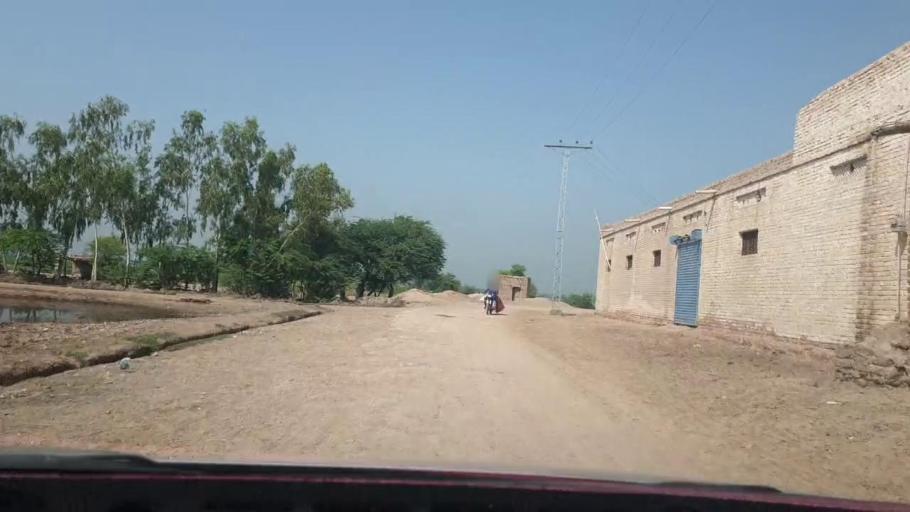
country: PK
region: Sindh
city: Nasirabad
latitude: 27.4239
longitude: 67.9065
